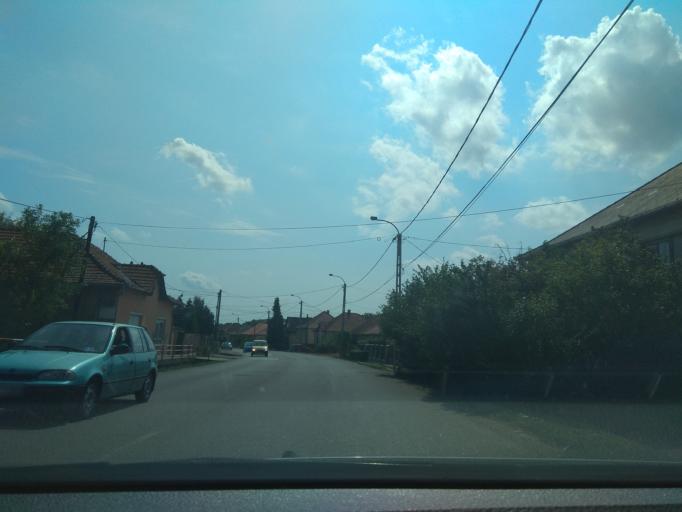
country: HU
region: Heves
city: Andornaktalya
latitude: 47.8576
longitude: 20.4067
